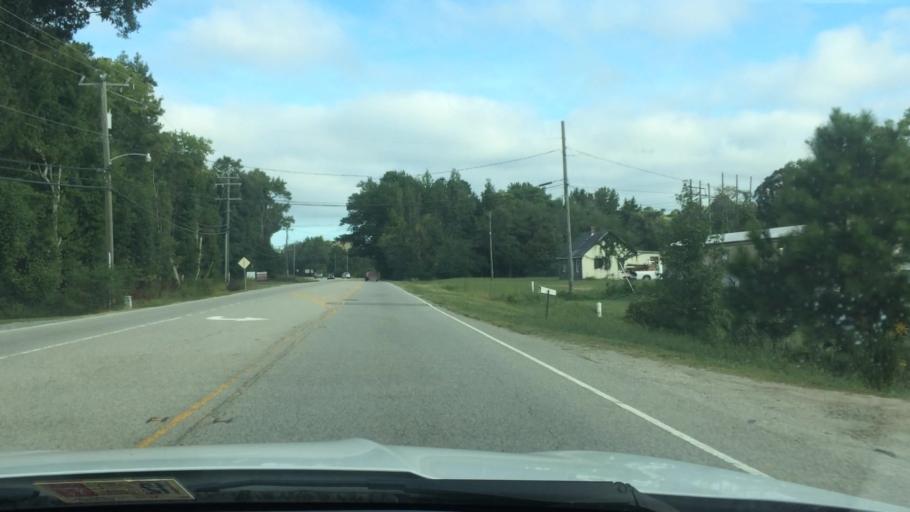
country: US
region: Virginia
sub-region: City of Williamsburg
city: Williamsburg
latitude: 37.2303
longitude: -76.6269
